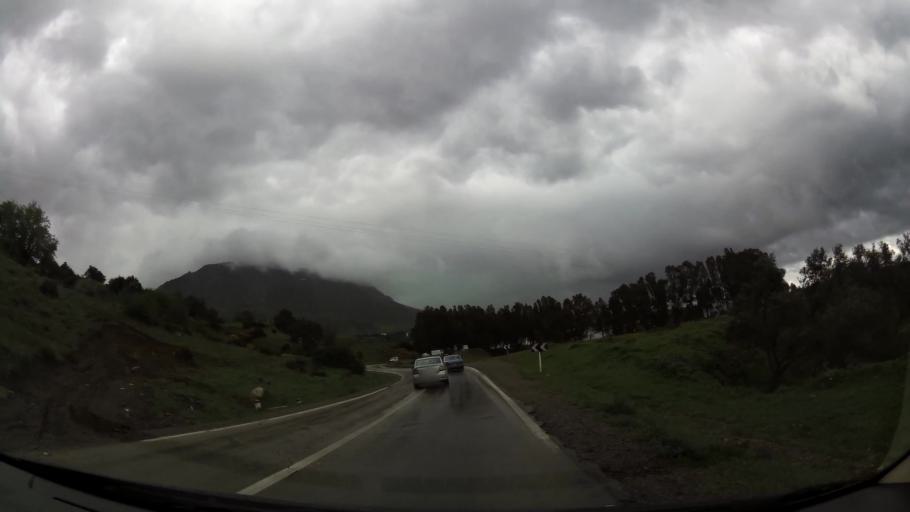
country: MA
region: Tanger-Tetouan
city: Chefchaouene
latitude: 35.1918
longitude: -5.2905
